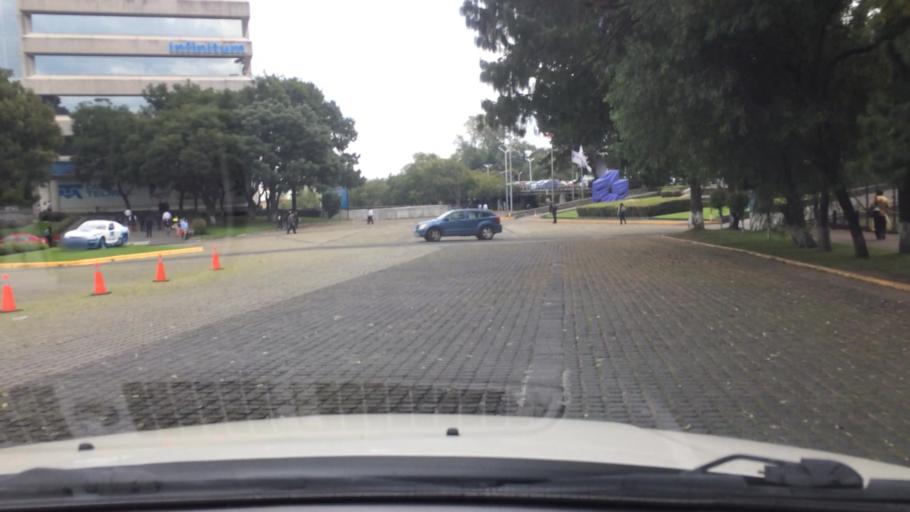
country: MX
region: Mexico City
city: Tlalpan
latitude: 19.2984
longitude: -99.1848
